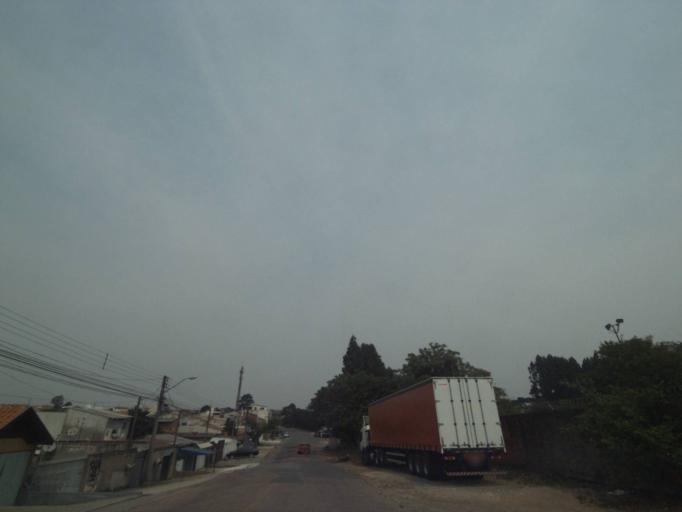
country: BR
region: Parana
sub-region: Sao Jose Dos Pinhais
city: Sao Jose dos Pinhais
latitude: -25.5186
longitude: -49.2890
